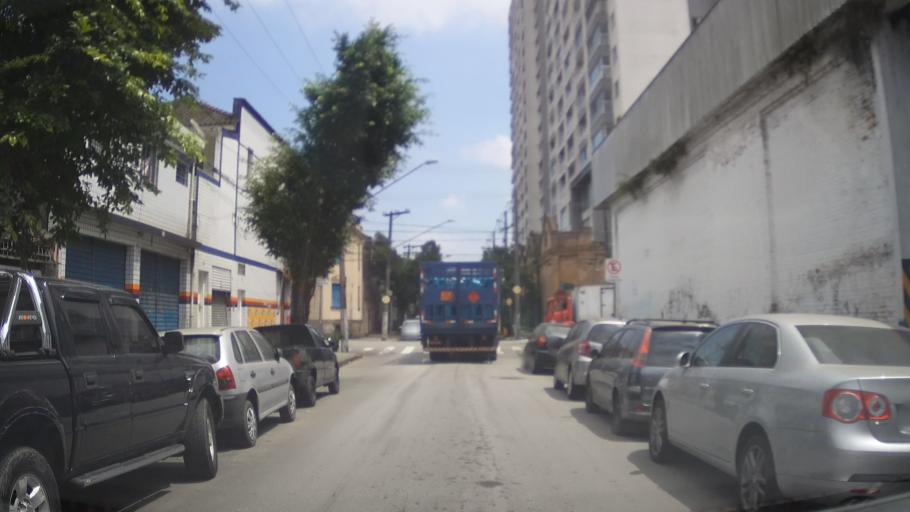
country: BR
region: Sao Paulo
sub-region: Santos
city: Santos
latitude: -23.9483
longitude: -46.3188
